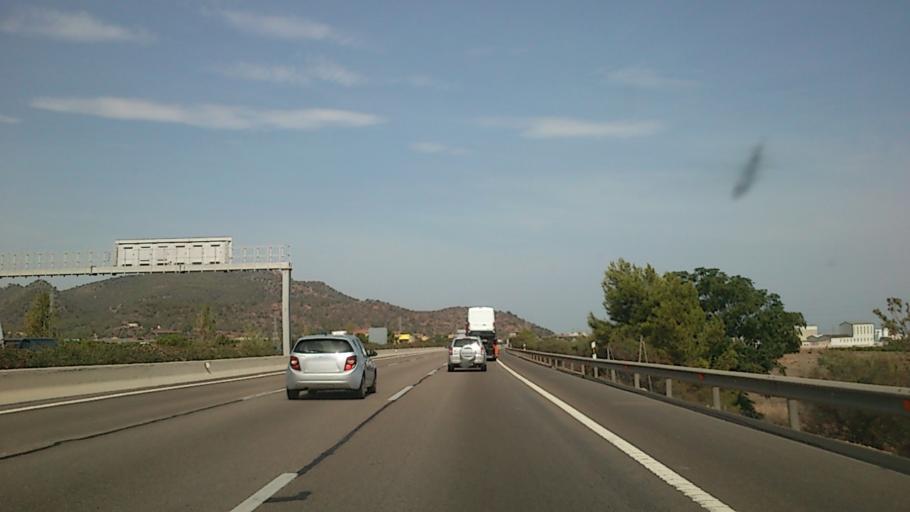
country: ES
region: Valencia
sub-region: Provincia de Valencia
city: Pucol
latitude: 39.6155
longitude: -0.3386
